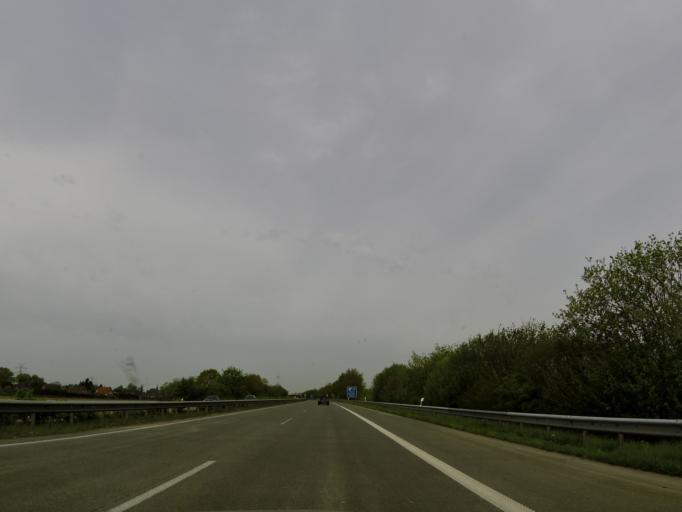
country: DE
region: Schleswig-Holstein
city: Klein Offenseth-Sparrieshoop
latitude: 53.7958
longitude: 9.6933
